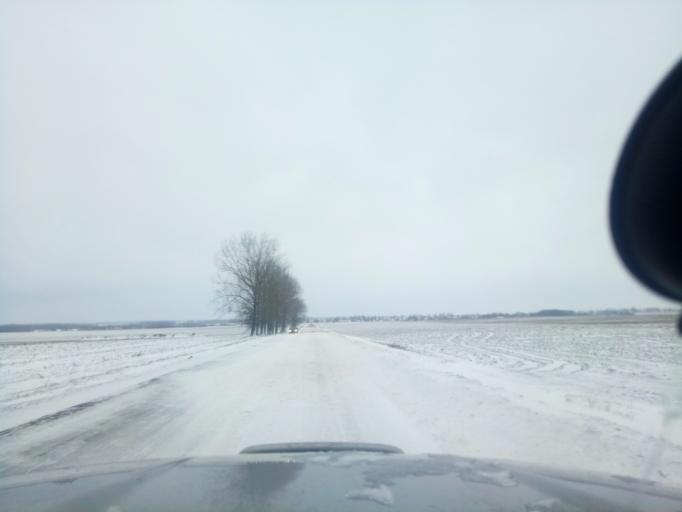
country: BY
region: Minsk
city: Tsimkavichy
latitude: 53.0563
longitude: 26.9539
